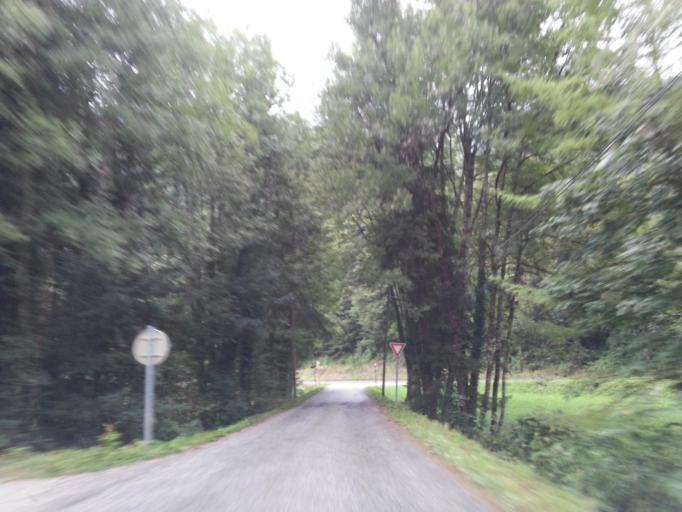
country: FR
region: Rhone-Alpes
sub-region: Departement de la Savoie
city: Marthod
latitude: 45.7141
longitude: 6.4807
